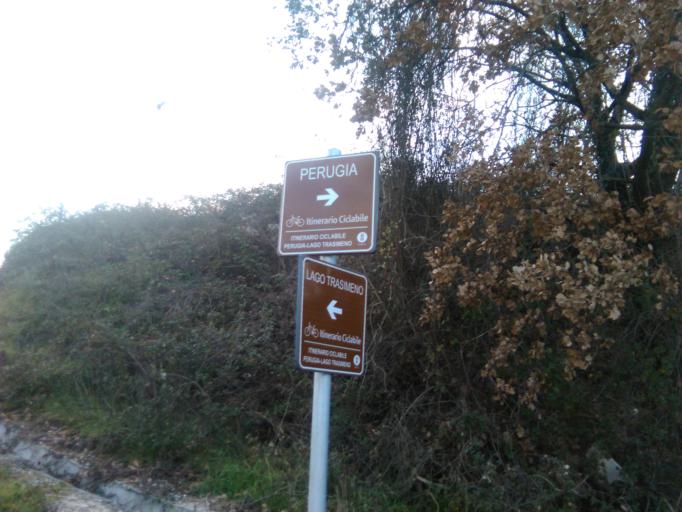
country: IT
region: Umbria
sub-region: Provincia di Perugia
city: Lacugnano
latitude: 43.0844
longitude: 12.3577
